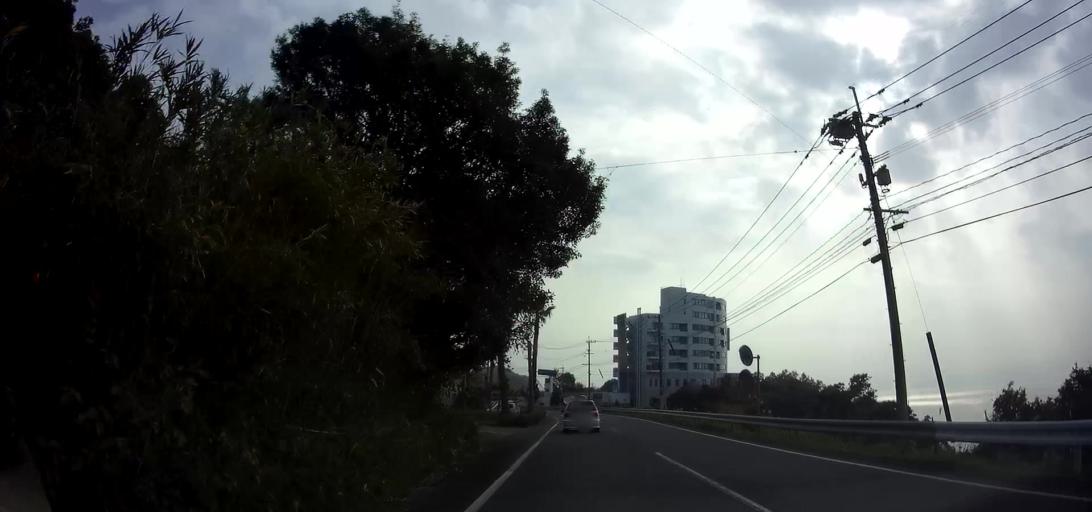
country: JP
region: Nagasaki
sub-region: Isahaya-shi
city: Isahaya
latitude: 32.7929
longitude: 130.1107
